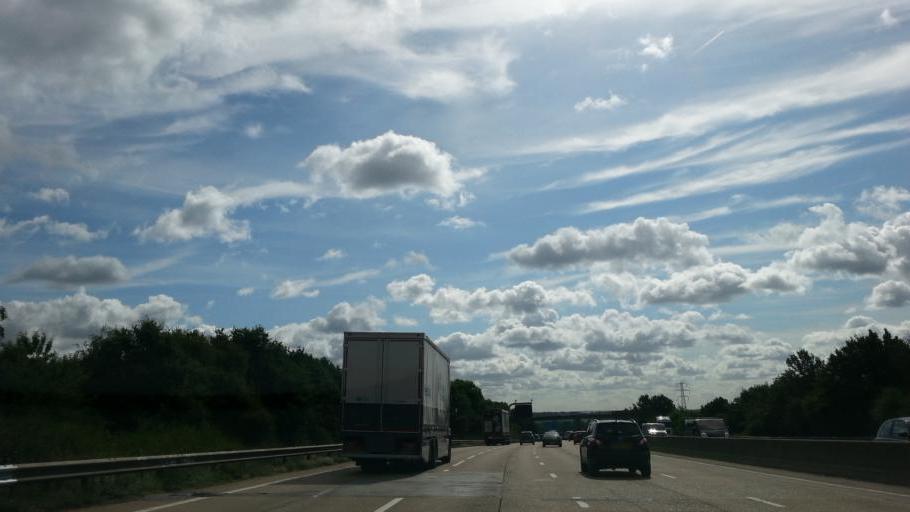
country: GB
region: England
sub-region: Greater London
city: Enfield
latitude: 51.6883
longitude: -0.0782
